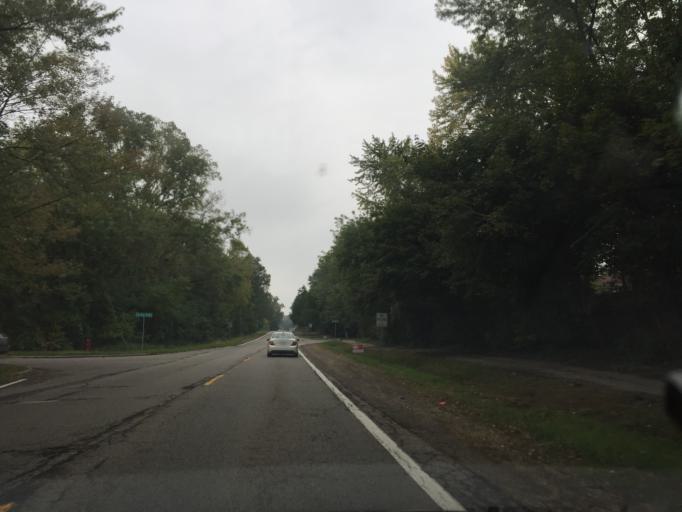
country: US
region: Michigan
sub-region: Oakland County
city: Orchard Lake
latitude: 42.5741
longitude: -83.3536
